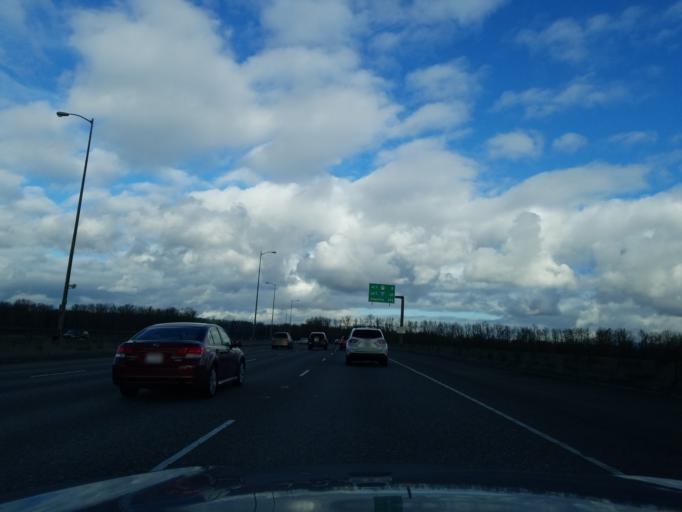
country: US
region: Washington
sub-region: Clark County
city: Mill Plain
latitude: 45.5754
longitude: -122.5454
